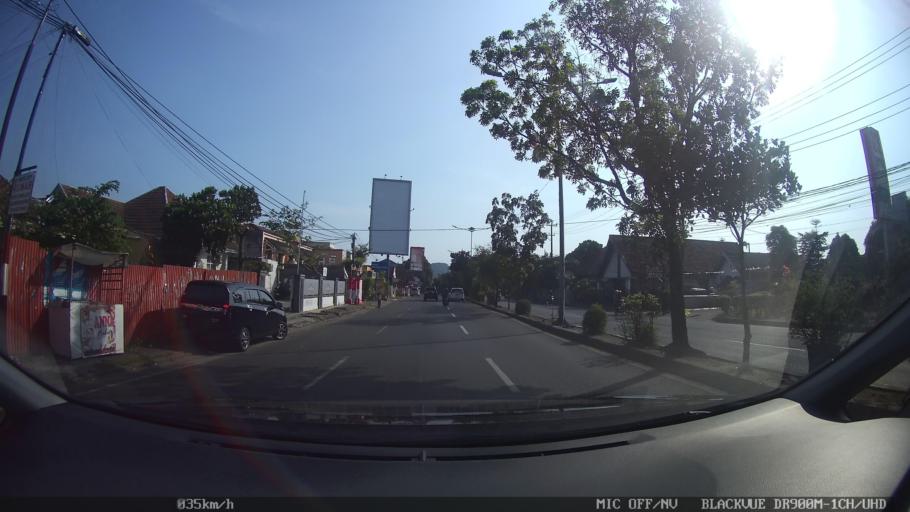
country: ID
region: Lampung
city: Bandarlampung
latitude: -5.4054
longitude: 105.2589
